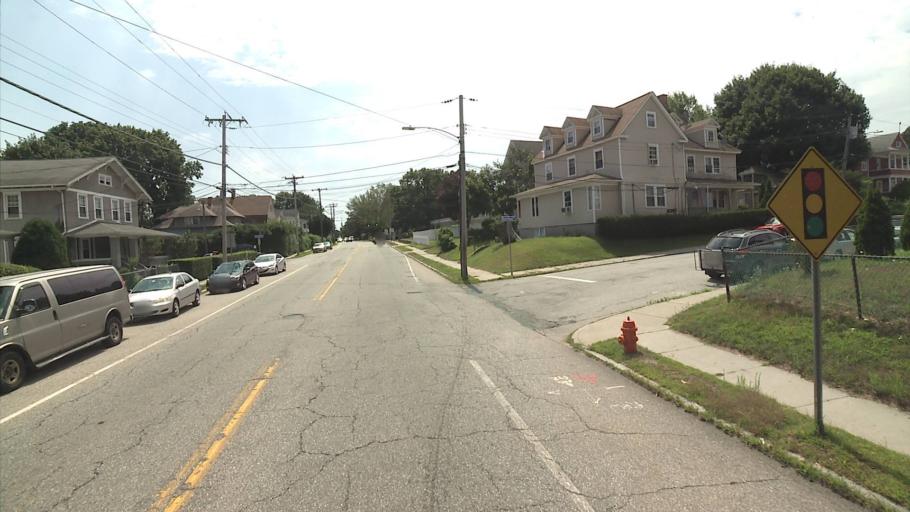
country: US
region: Connecticut
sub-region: New London County
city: New London
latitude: 41.3435
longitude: -72.1083
